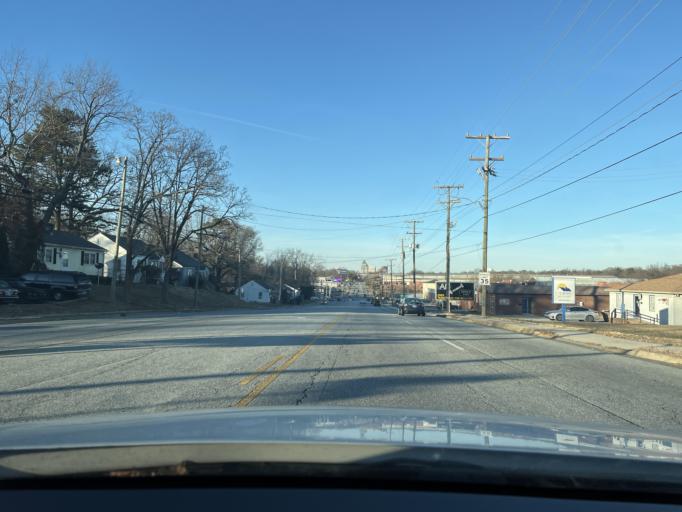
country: US
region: North Carolina
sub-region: Guilford County
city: Greensboro
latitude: 36.0451
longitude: -79.7915
